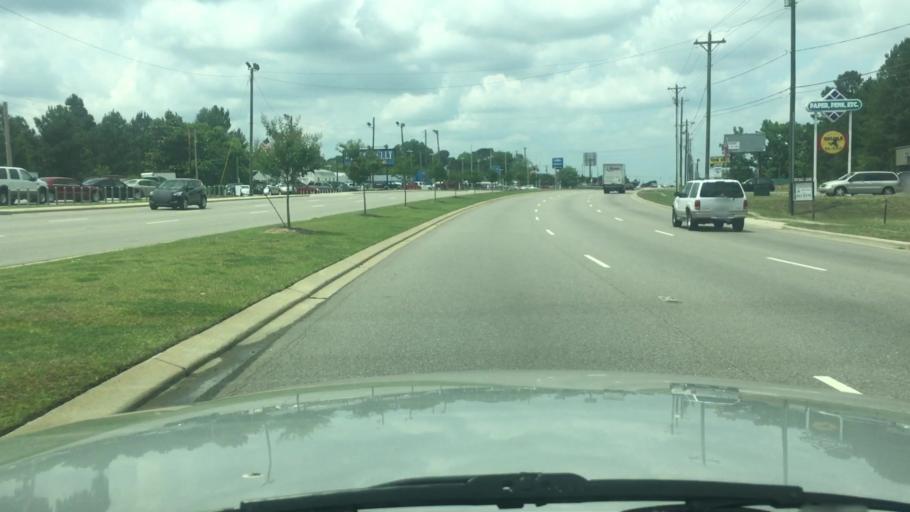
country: US
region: North Carolina
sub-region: Cumberland County
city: Fort Bragg
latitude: 35.0886
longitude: -78.9530
